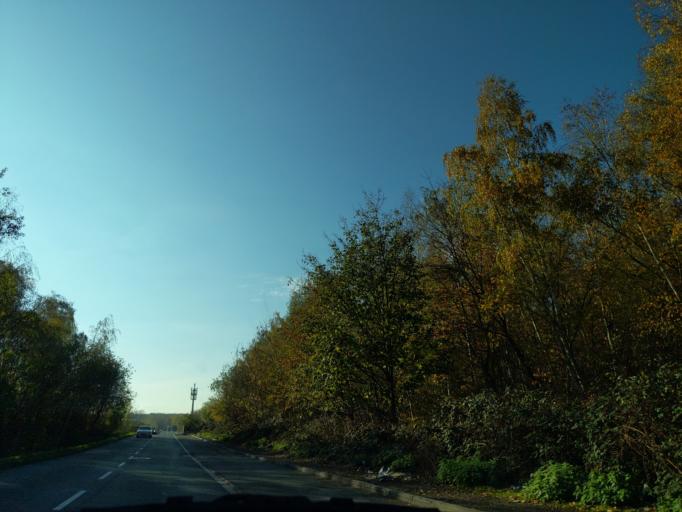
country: DE
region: North Rhine-Westphalia
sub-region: Regierungsbezirk Koln
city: Bilderstoeckchen
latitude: 51.0182
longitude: 6.9338
